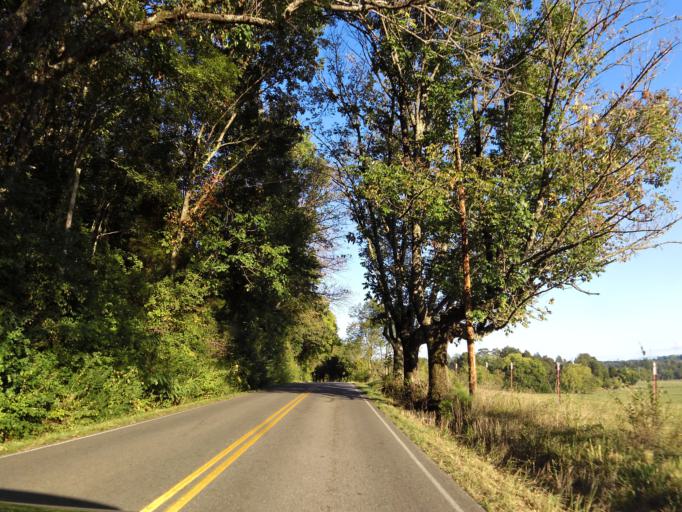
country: US
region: Tennessee
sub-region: Blount County
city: Eagleton Village
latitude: 35.8208
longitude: -83.9303
